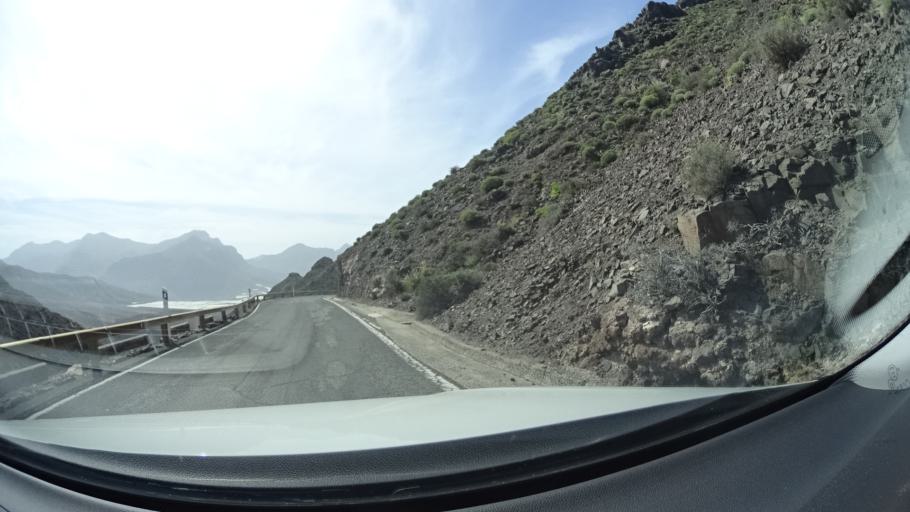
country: ES
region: Canary Islands
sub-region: Provincia de Las Palmas
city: San Nicolas
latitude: 28.0189
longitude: -15.7853
